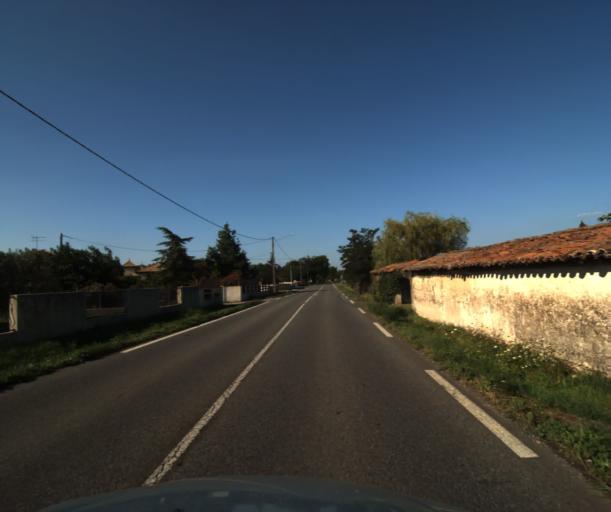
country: FR
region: Midi-Pyrenees
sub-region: Departement de la Haute-Garonne
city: Labarthe-sur-Leze
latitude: 43.4378
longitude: 1.3789
